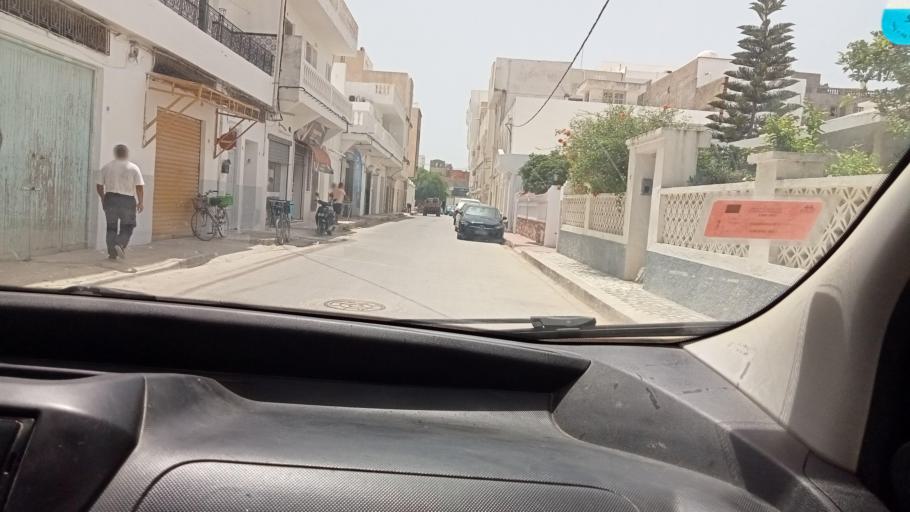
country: TN
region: Nabul
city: Qulaybiyah
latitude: 36.8501
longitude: 11.0877
